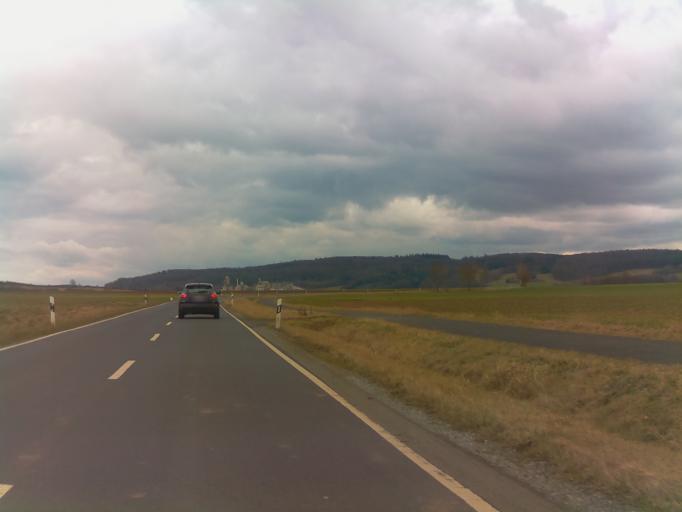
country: DE
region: Hesse
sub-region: Regierungsbezirk Kassel
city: Bad Salzschlirf
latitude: 50.6075
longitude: 9.5075
